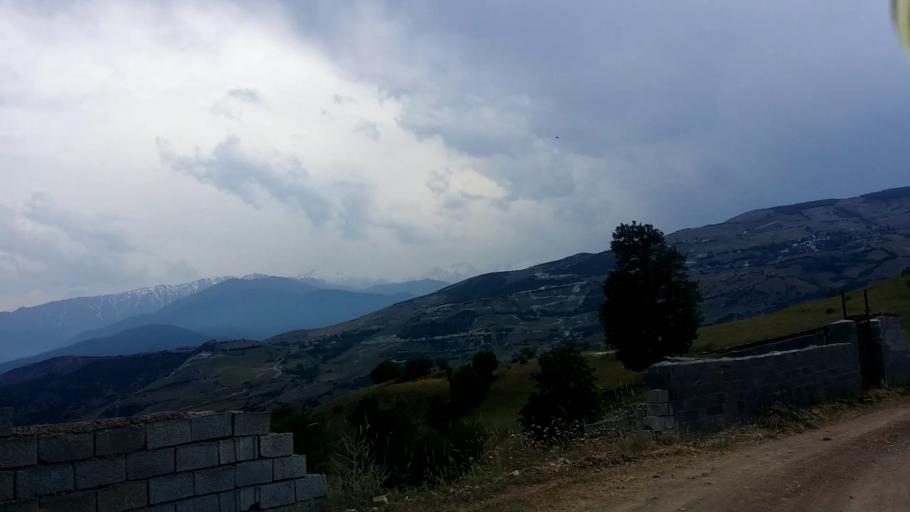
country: IR
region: Mazandaran
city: Chalus
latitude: 36.5530
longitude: 51.2934
